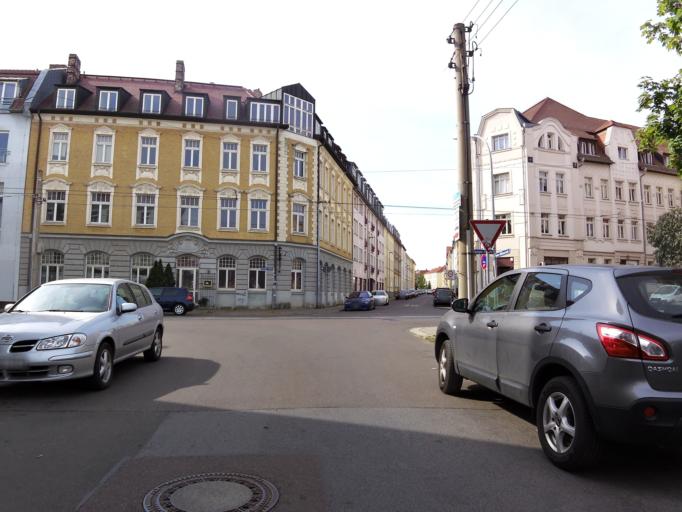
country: DE
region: Saxony
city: Schkeuditz
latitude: 51.3599
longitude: 12.2905
